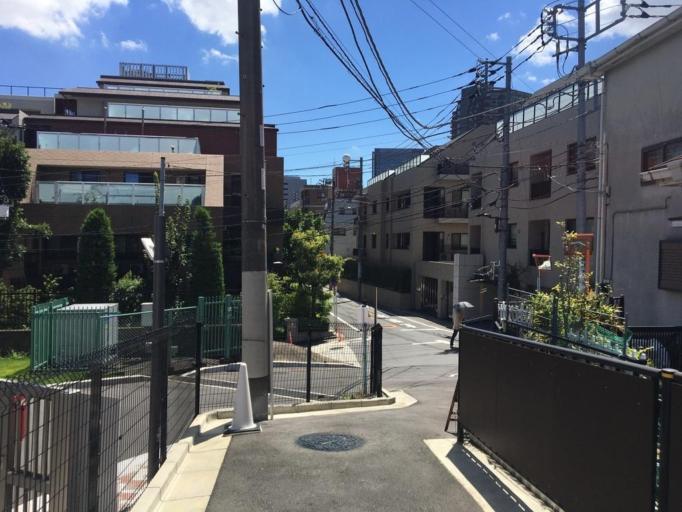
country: JP
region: Tokyo
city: Tokyo
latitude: 35.7048
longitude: 139.7374
